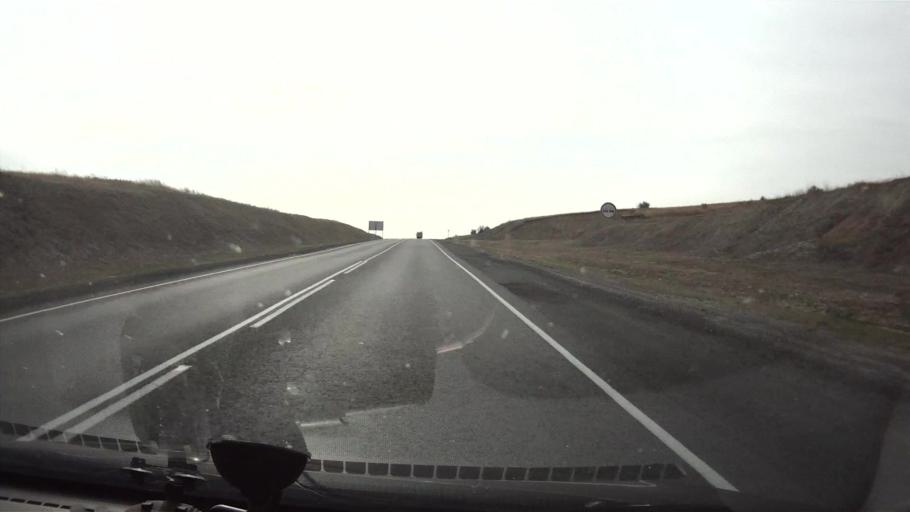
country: RU
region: Saratov
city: Sennoy
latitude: 52.1387
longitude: 46.8814
